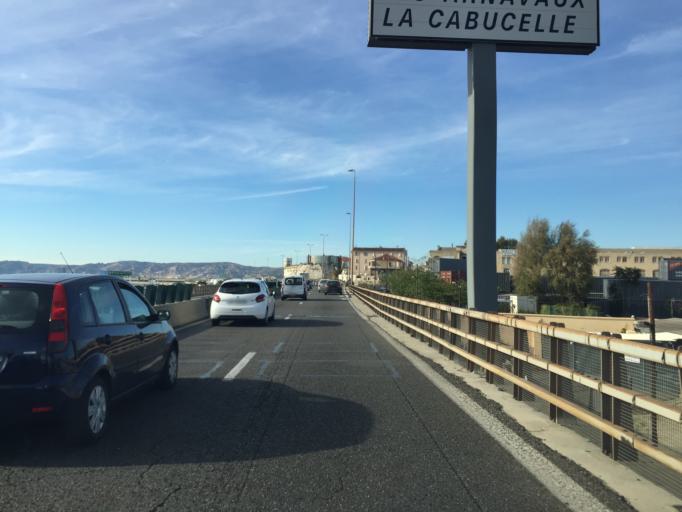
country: FR
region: Provence-Alpes-Cote d'Azur
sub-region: Departement des Bouches-du-Rhone
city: Marseille 03
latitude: 43.3242
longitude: 5.3625
